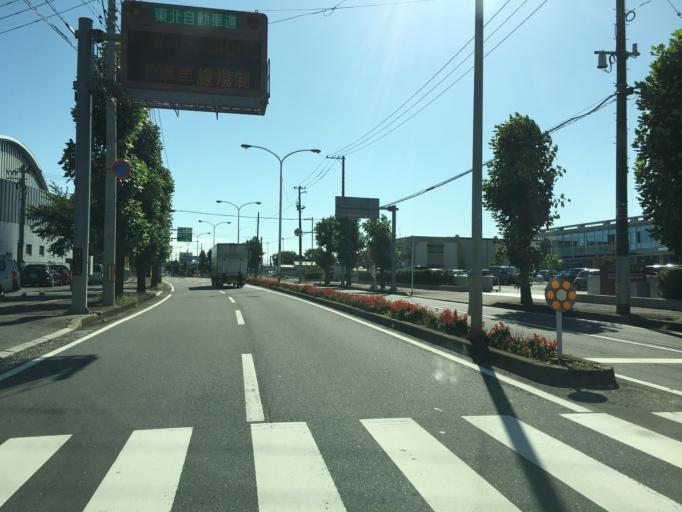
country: JP
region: Fukushima
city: Sukagawa
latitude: 37.2930
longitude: 140.3561
